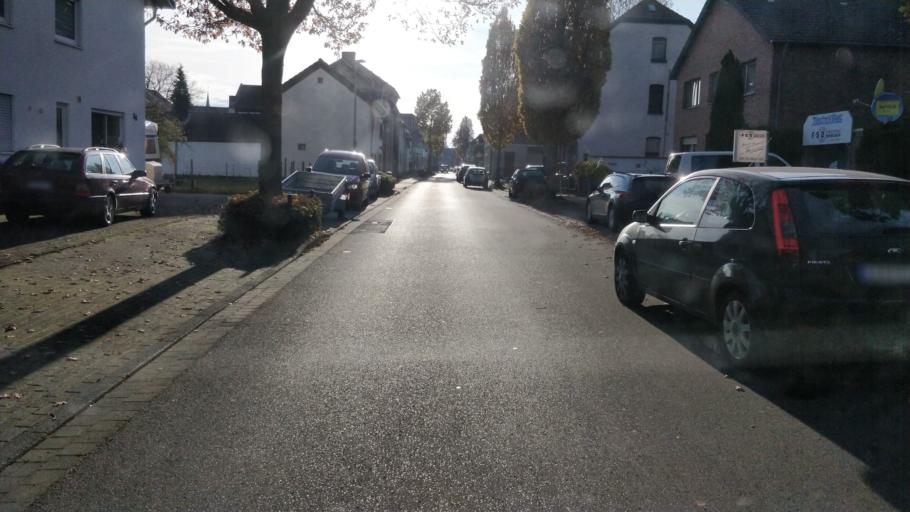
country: DE
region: North Rhine-Westphalia
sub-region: Regierungsbezirk Koln
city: Euskirchen
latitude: 50.6274
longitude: 6.8523
